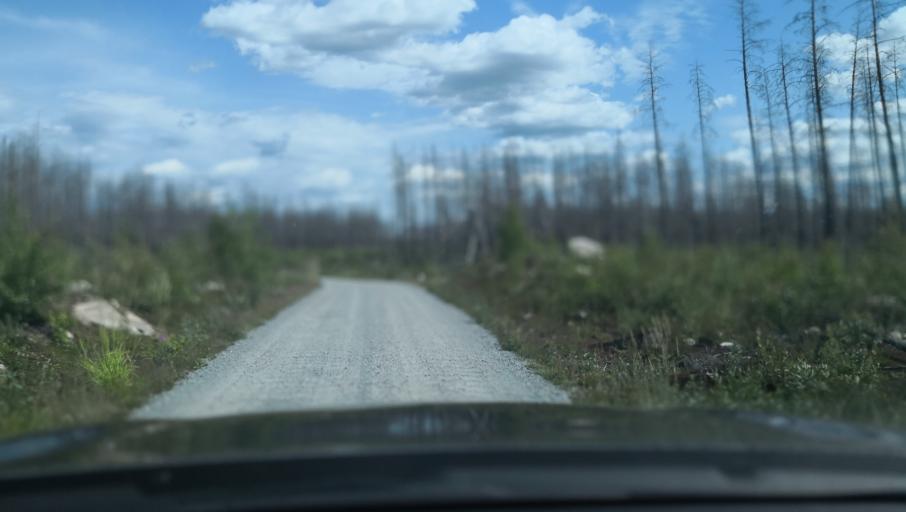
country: SE
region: Vaestmanland
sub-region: Surahammars Kommun
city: Ramnas
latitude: 59.8977
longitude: 16.1153
